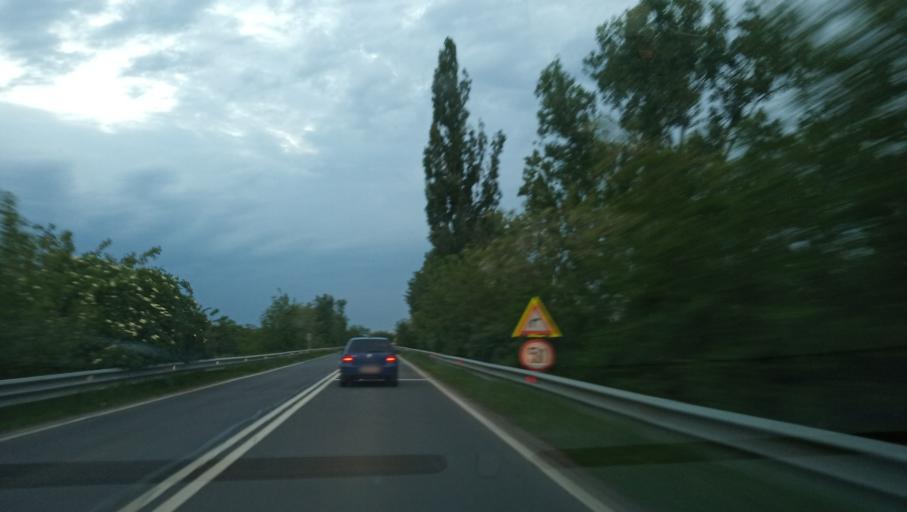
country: RO
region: Timis
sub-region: Comuna Sag
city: Sag
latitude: 45.6373
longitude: 21.1825
